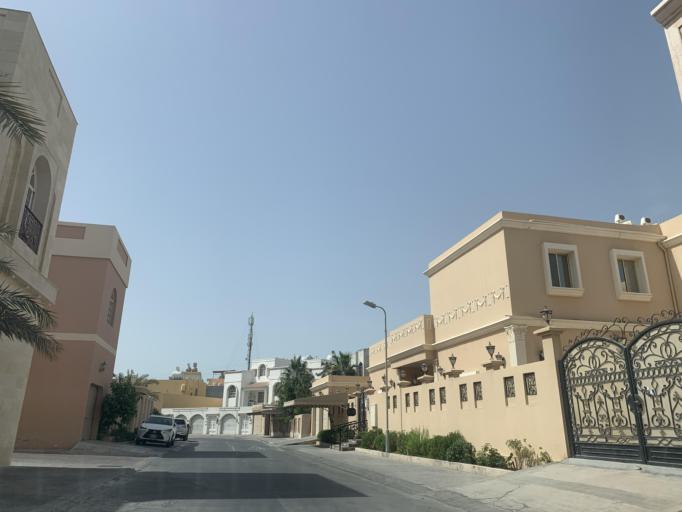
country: BH
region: Northern
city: Ar Rifa'
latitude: 26.1433
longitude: 50.5688
